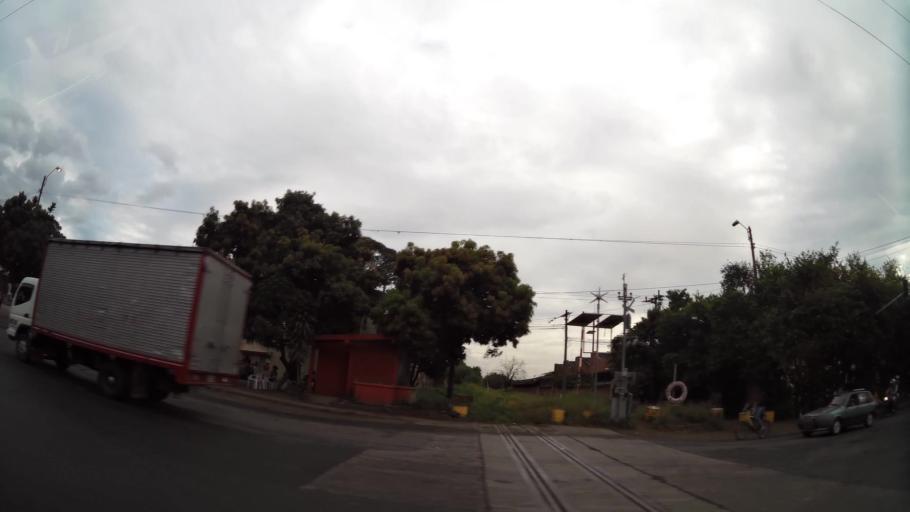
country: CO
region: Valle del Cauca
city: Cali
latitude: 3.4929
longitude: -76.5175
